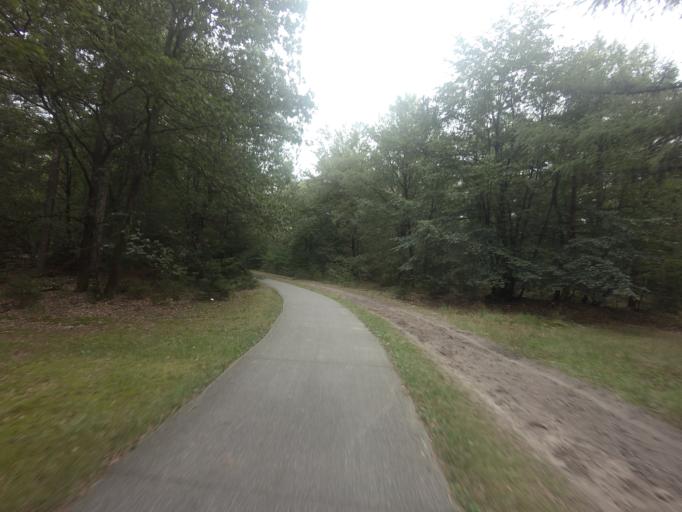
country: NL
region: Drenthe
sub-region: Gemeente Westerveld
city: Dwingeloo
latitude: 52.8949
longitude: 6.2949
